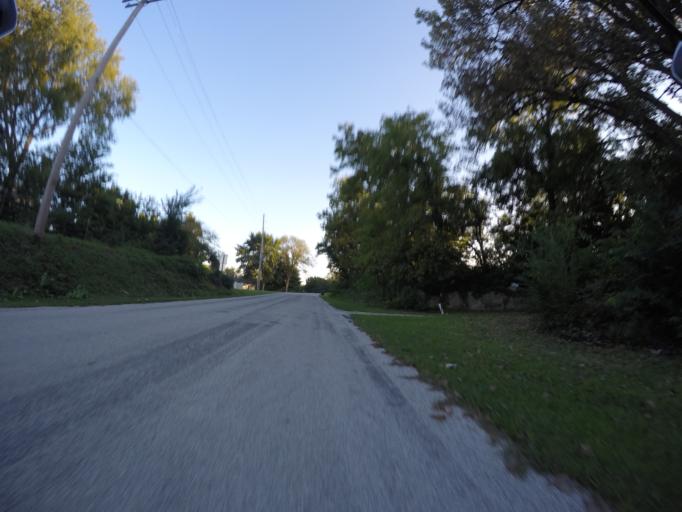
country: US
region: Kansas
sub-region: Riley County
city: Ogden
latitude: 39.1185
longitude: -96.7114
